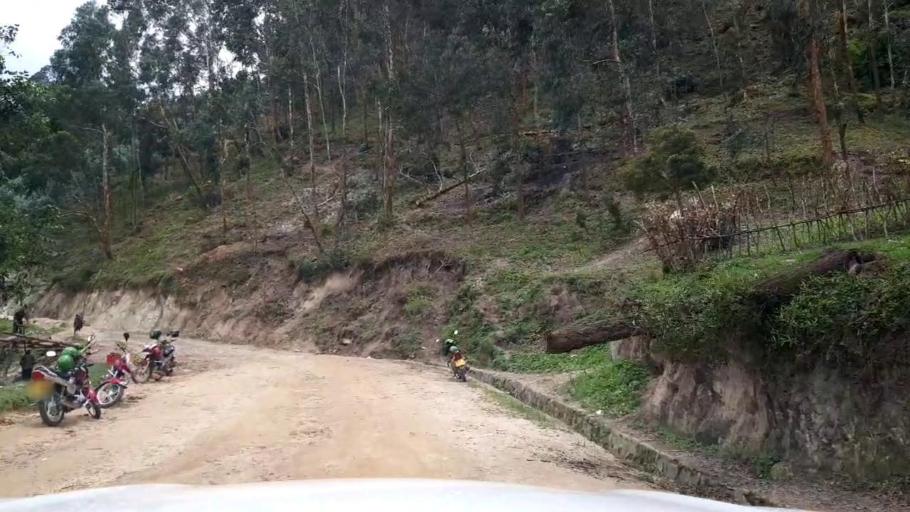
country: RW
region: Western Province
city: Kibuye
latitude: -1.9669
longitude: 29.3952
